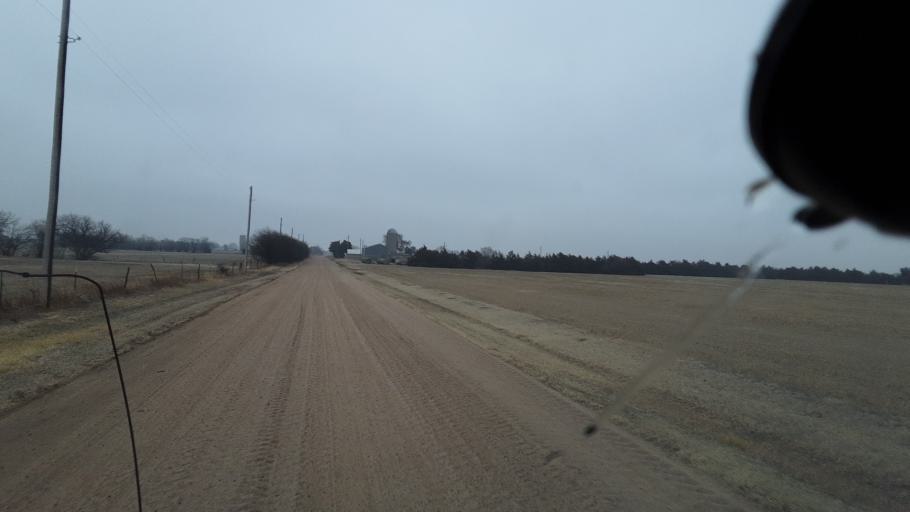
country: US
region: Kansas
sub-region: Reno County
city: South Hutchinson
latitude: 37.9845
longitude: -98.0017
